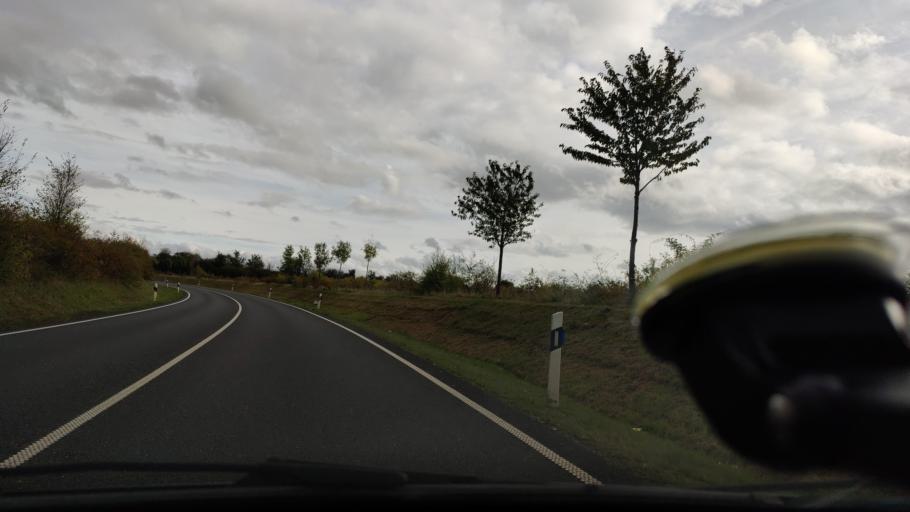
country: DE
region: North Rhine-Westphalia
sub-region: Regierungsbezirk Koln
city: Heinsberg
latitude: 51.0471
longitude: 6.0875
